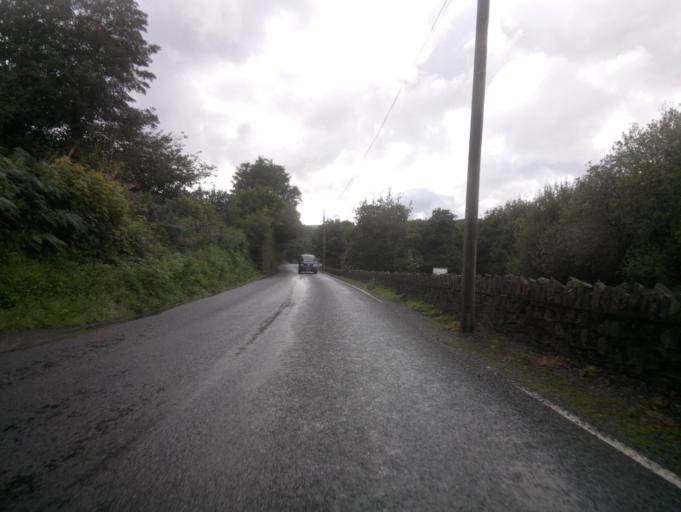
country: GB
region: England
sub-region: Devon
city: South Brent
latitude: 50.4149
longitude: -3.8369
